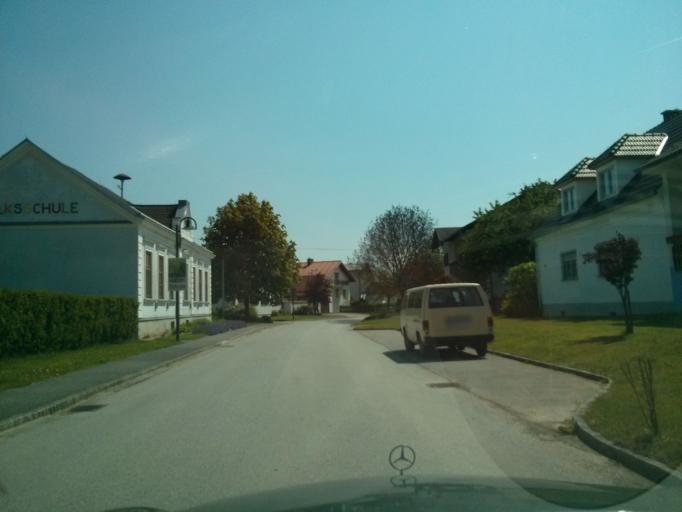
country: AT
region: Burgenland
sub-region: Politischer Bezirk Oberwart
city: Bad Tatzmannsdorf
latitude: 47.3177
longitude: 16.2048
